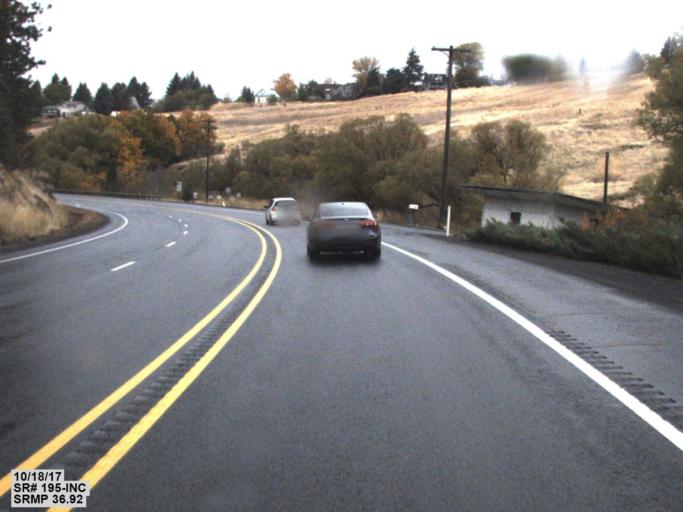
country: US
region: Washington
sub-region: Whitman County
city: Colfax
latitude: 46.8717
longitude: -117.3554
